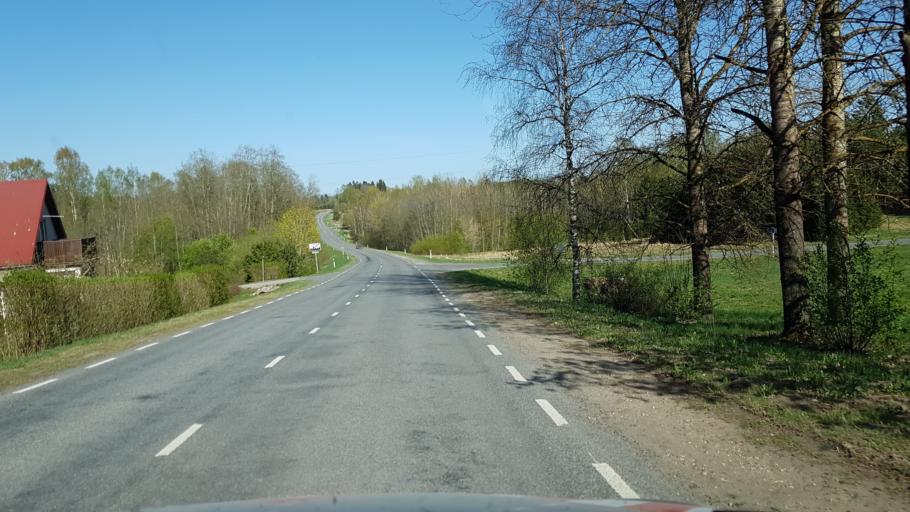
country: EE
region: Viljandimaa
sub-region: Viljandi linn
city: Viljandi
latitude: 58.3082
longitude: 25.5409
